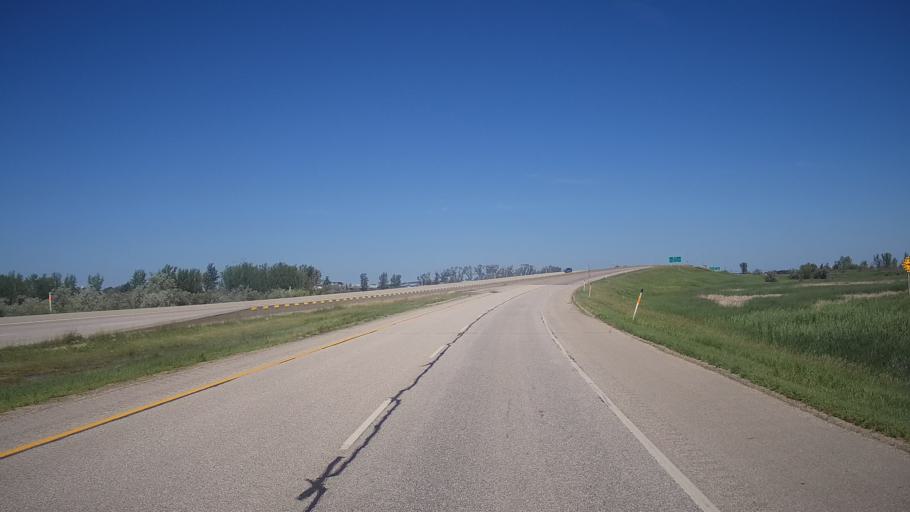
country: CA
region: Manitoba
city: Portage la Prairie
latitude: 49.9636
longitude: -98.3538
